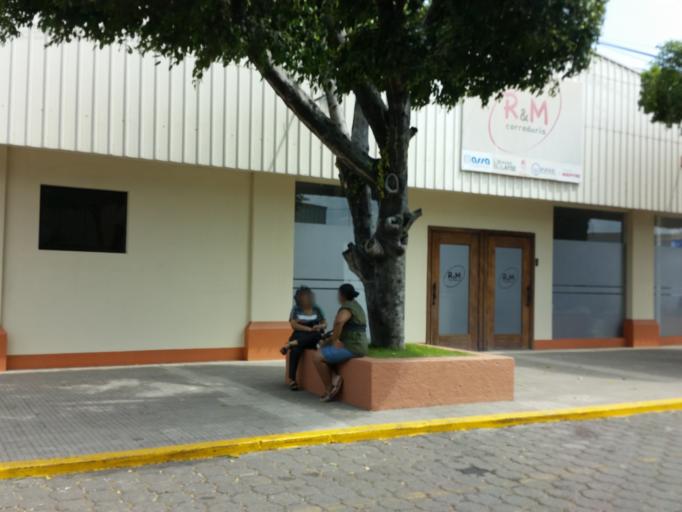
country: NI
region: Managua
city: Managua
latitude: 12.1110
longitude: -86.2545
